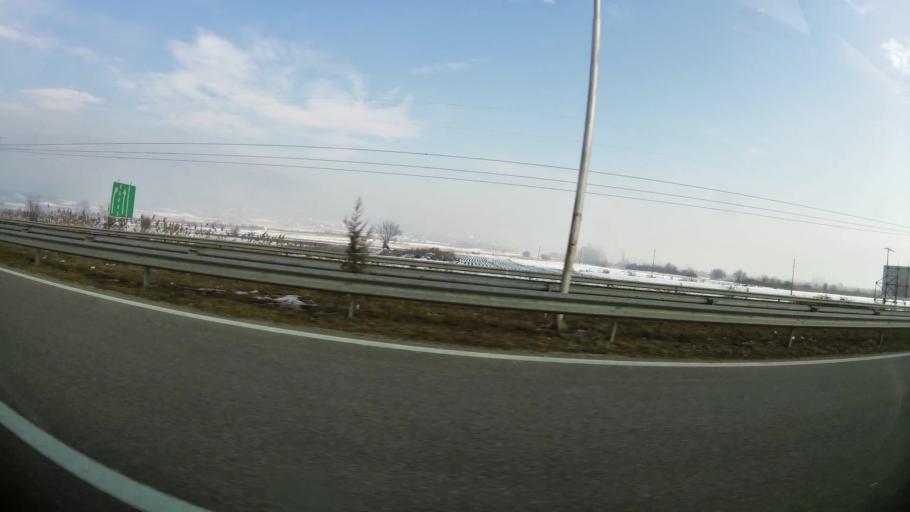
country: MK
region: Aracinovo
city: Arachinovo
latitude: 42.0230
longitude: 21.5321
